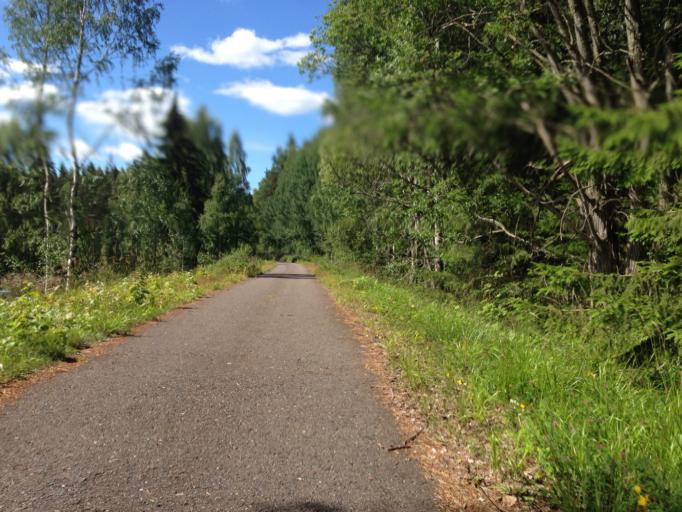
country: SE
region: Dalarna
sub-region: Ludvika Kommun
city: Ludvika
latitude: 60.1991
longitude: 15.0823
